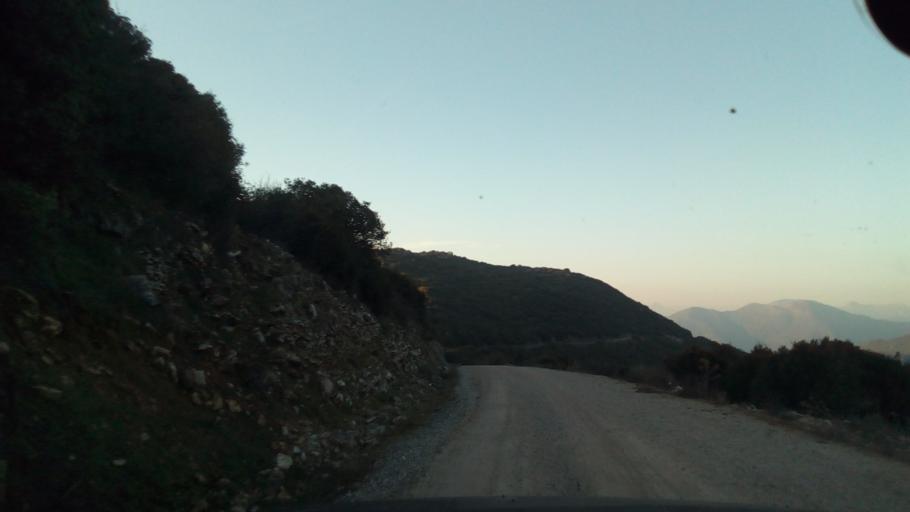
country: GR
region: West Greece
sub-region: Nomos Aitolias kai Akarnanias
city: Nafpaktos
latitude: 38.4674
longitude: 21.8248
